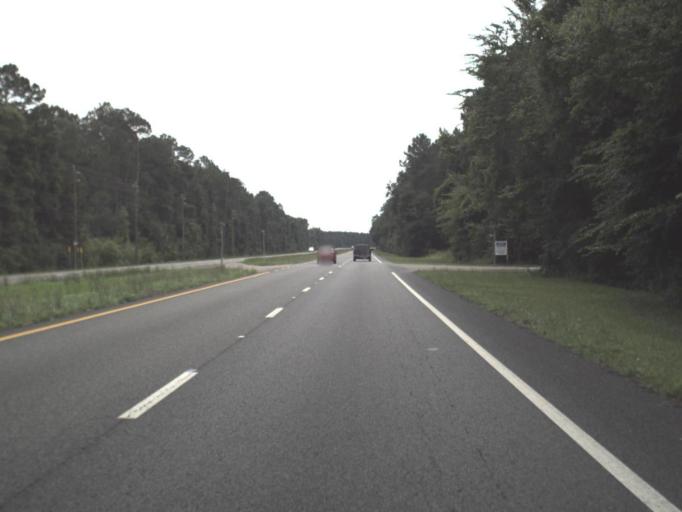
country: US
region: Florida
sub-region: Nassau County
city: Hilliard
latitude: 30.6377
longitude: -81.8612
